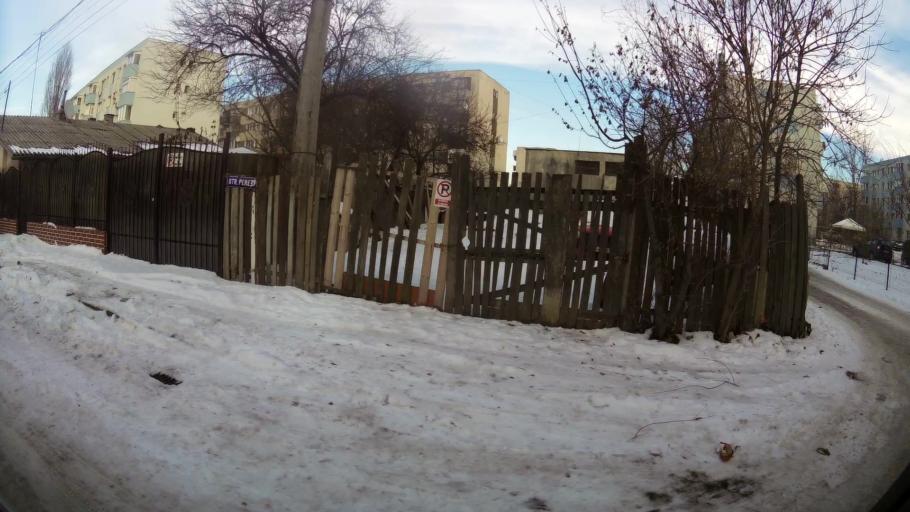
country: RO
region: Bucuresti
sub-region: Municipiul Bucuresti
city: Bucuresti
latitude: 44.3911
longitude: 26.0730
